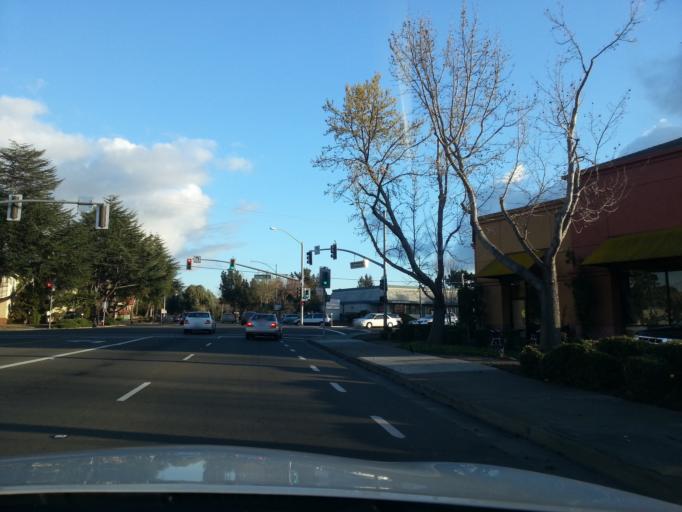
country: US
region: California
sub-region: Santa Clara County
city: Los Altos
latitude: 37.4033
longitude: -122.1065
